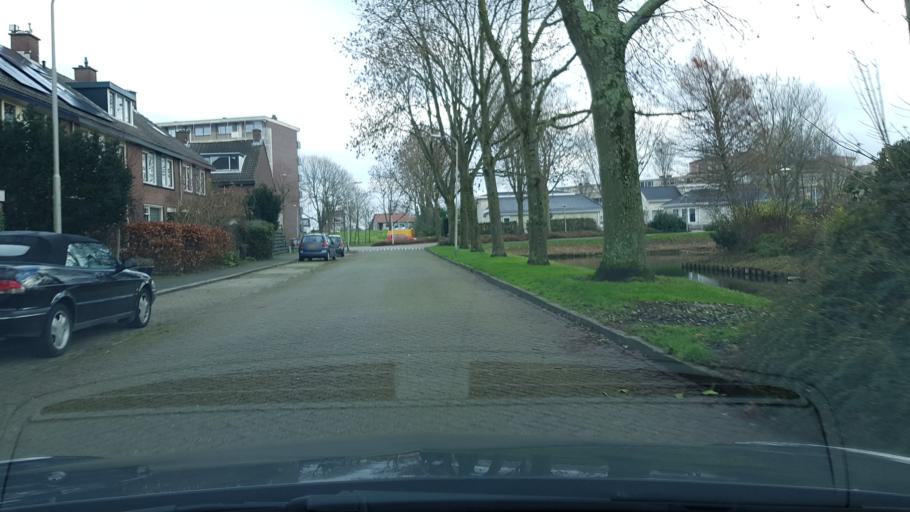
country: NL
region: South Holland
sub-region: Gemeente Lisse
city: Lisse
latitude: 52.2431
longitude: 4.5626
